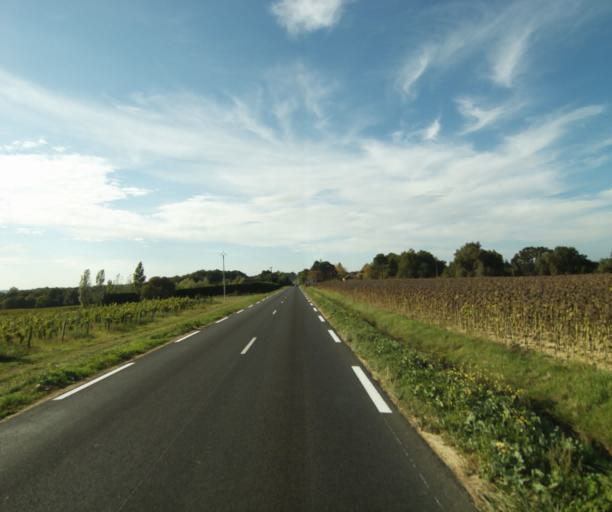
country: FR
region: Midi-Pyrenees
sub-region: Departement du Gers
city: Eauze
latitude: 43.8666
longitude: 0.0530
